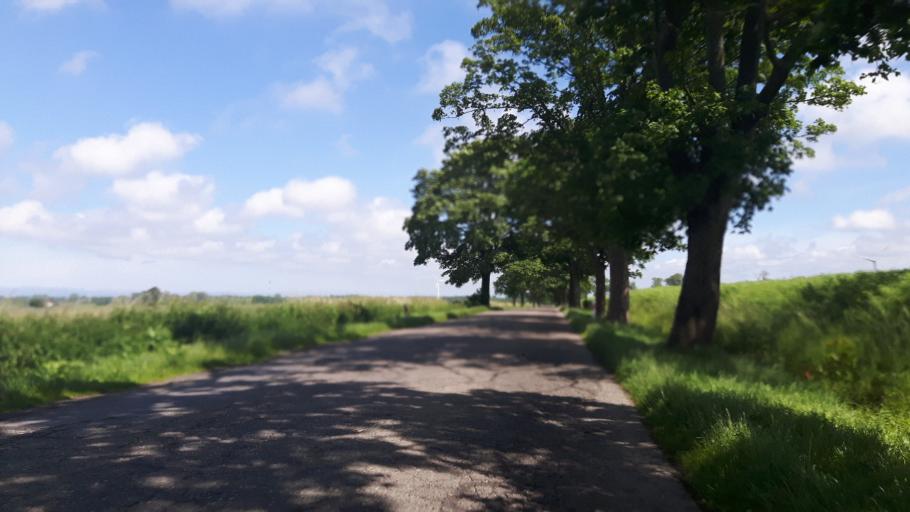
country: PL
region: Pomeranian Voivodeship
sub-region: Powiat slupski
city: Ustka
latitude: 54.5243
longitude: 16.7962
